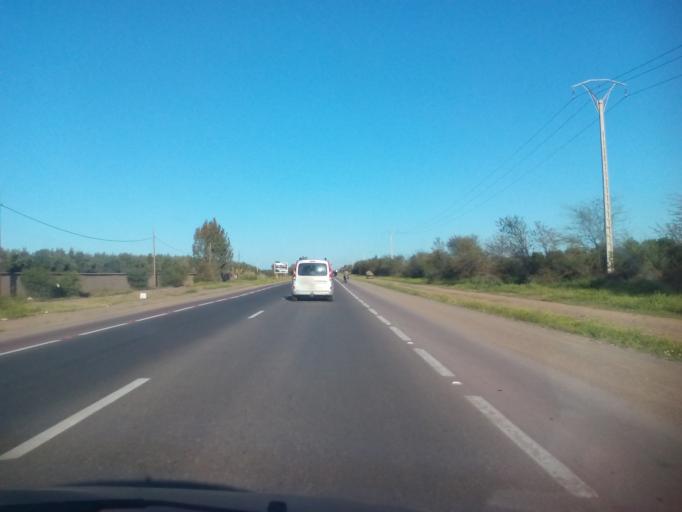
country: MA
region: Marrakech-Tensift-Al Haouz
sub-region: Marrakech
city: Marrakesh
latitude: 31.6302
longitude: -8.1569
